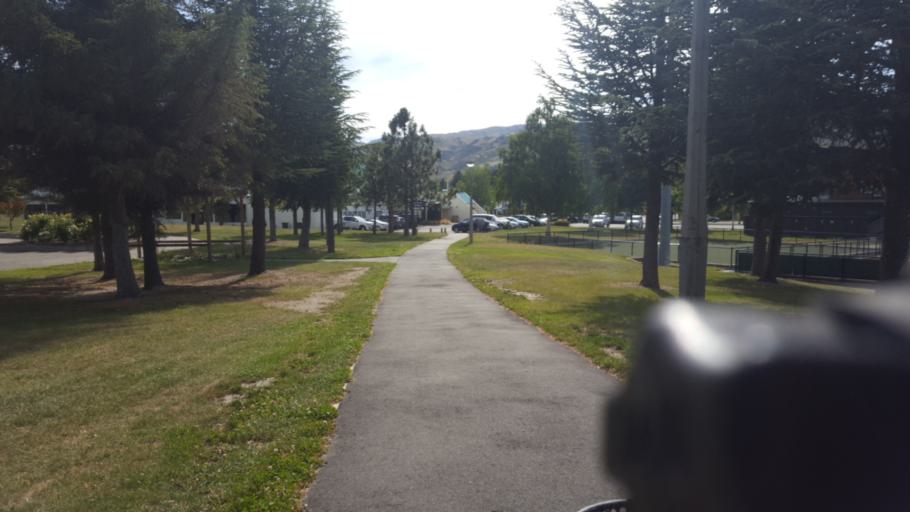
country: NZ
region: Otago
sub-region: Queenstown-Lakes District
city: Wanaka
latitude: -45.0393
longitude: 169.1961
